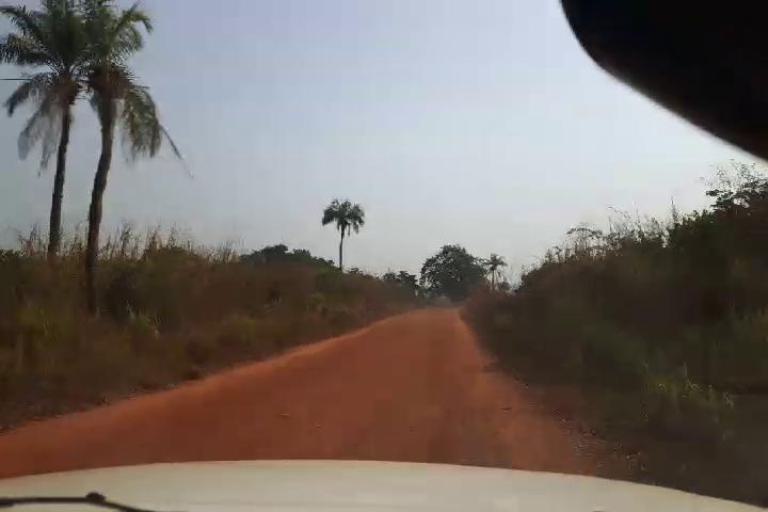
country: SL
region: Northern Province
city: Masingbi
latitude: 8.8521
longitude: -11.8270
